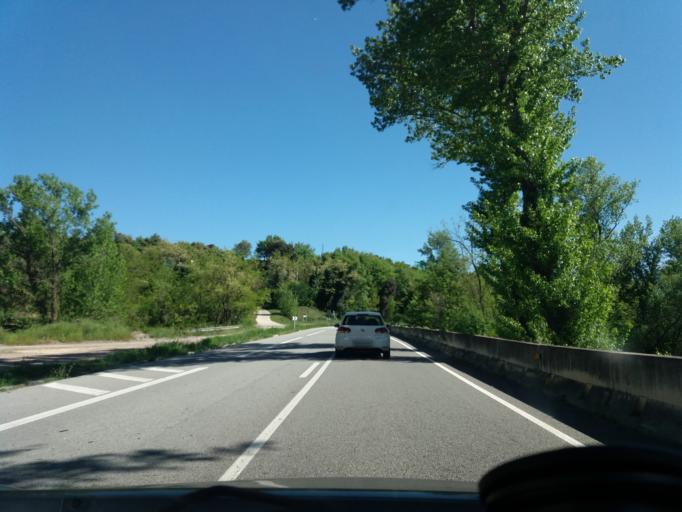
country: ES
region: Catalonia
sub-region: Provincia de Barcelona
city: Gironella
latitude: 42.0563
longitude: 1.8735
